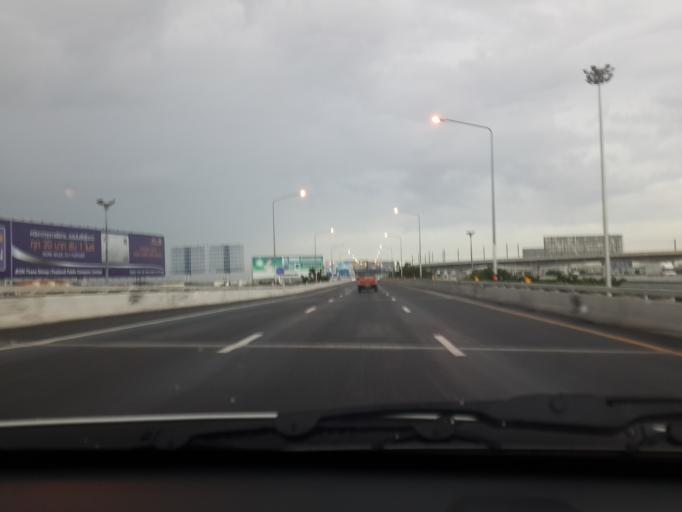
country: TH
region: Bangkok
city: Lat Krabang
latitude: 13.7308
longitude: 100.7595
